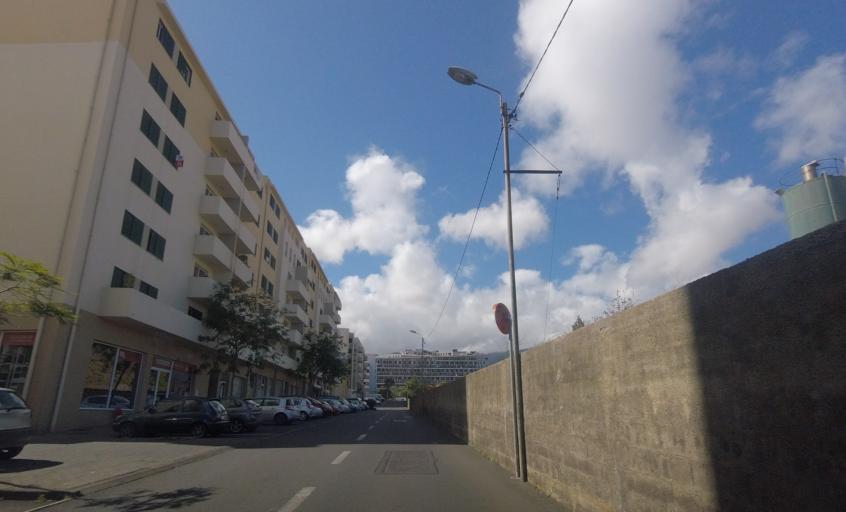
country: PT
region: Madeira
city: Camara de Lobos
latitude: 32.6461
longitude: -16.9399
